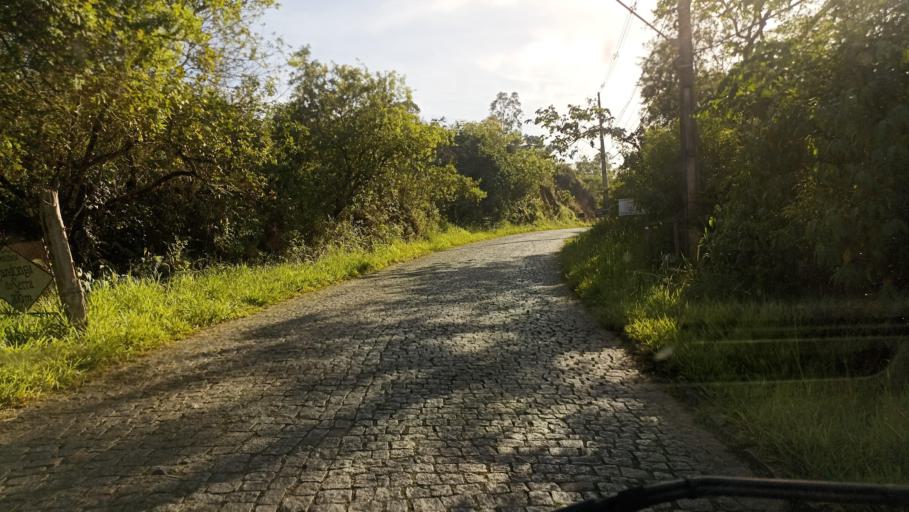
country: BR
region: Minas Gerais
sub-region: Tiradentes
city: Tiradentes
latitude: -21.1127
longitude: -44.1900
